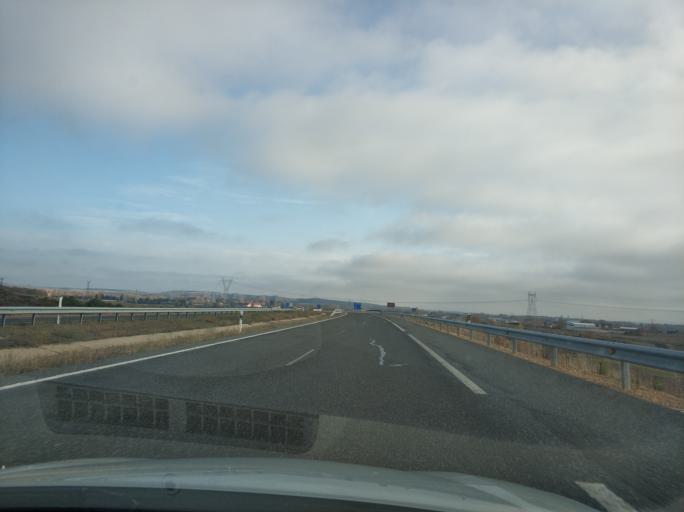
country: ES
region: Castille and Leon
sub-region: Provincia de Leon
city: Valdefresno
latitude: 42.5585
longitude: -5.4727
